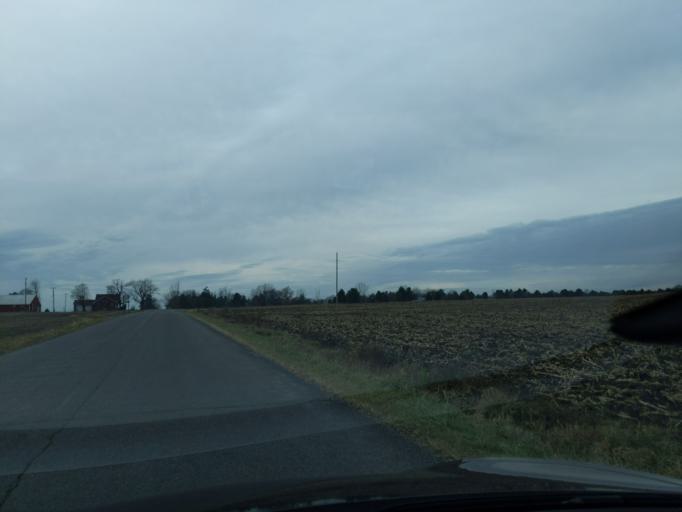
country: US
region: Michigan
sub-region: Ingham County
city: Williamston
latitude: 42.6542
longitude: -84.3647
